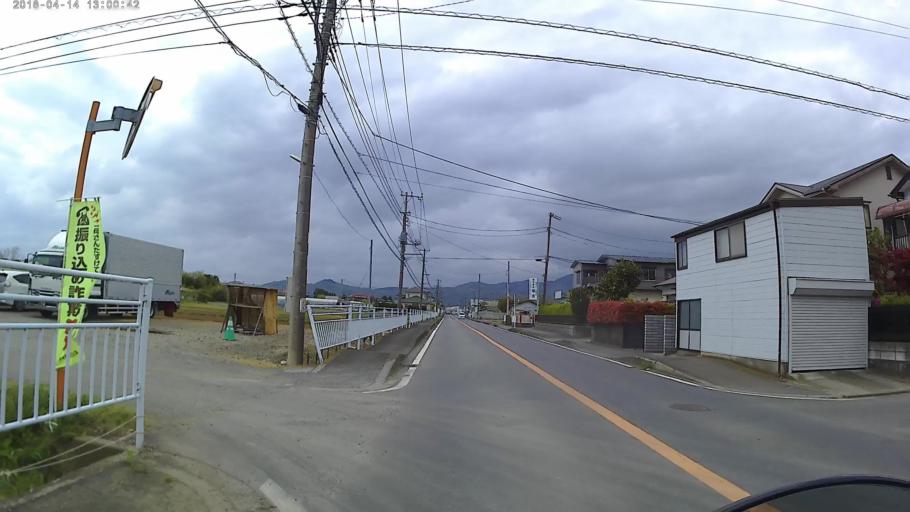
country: JP
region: Kanagawa
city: Isehara
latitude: 35.3730
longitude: 139.3025
